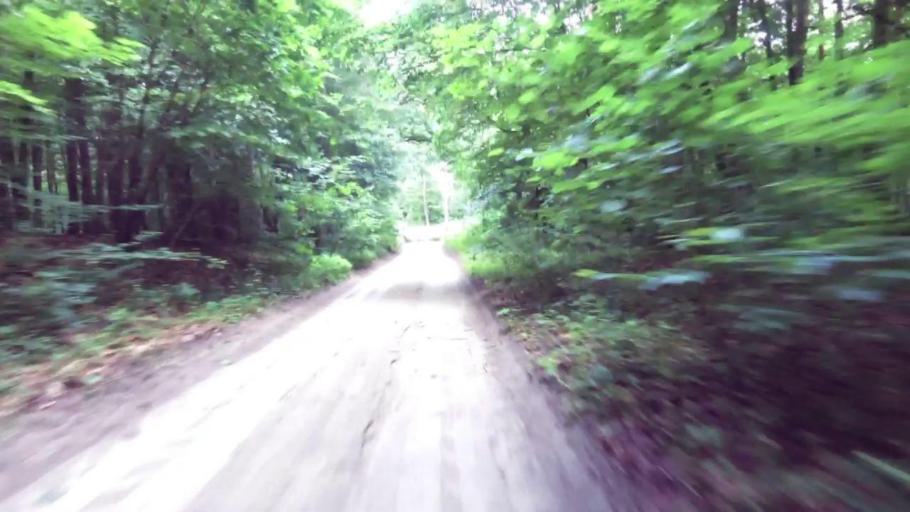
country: PL
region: West Pomeranian Voivodeship
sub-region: Powiat pyrzycki
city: Lipiany
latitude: 52.9784
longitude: 14.9242
